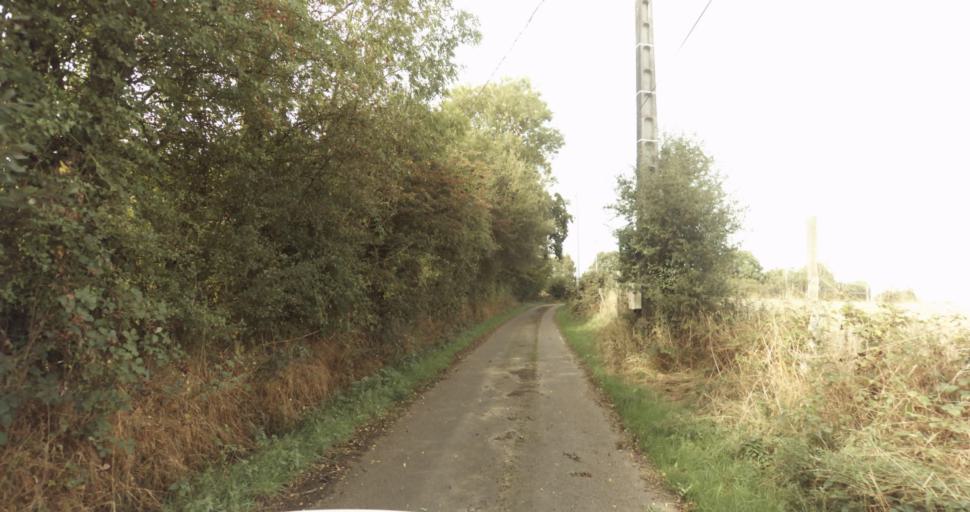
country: FR
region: Lower Normandy
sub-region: Departement de l'Orne
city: Gace
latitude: 48.7985
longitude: 0.3553
